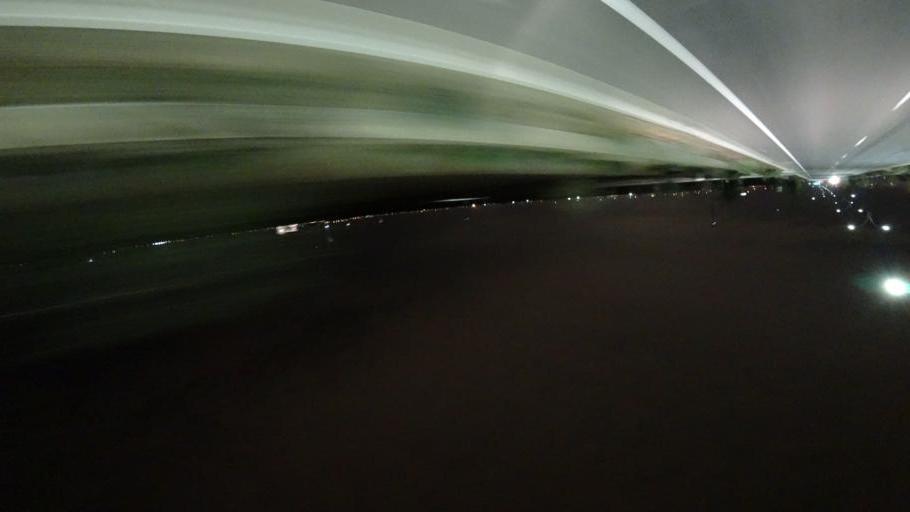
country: US
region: Arizona
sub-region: Maricopa County
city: Queen Creek
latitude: 33.3215
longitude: -111.6206
